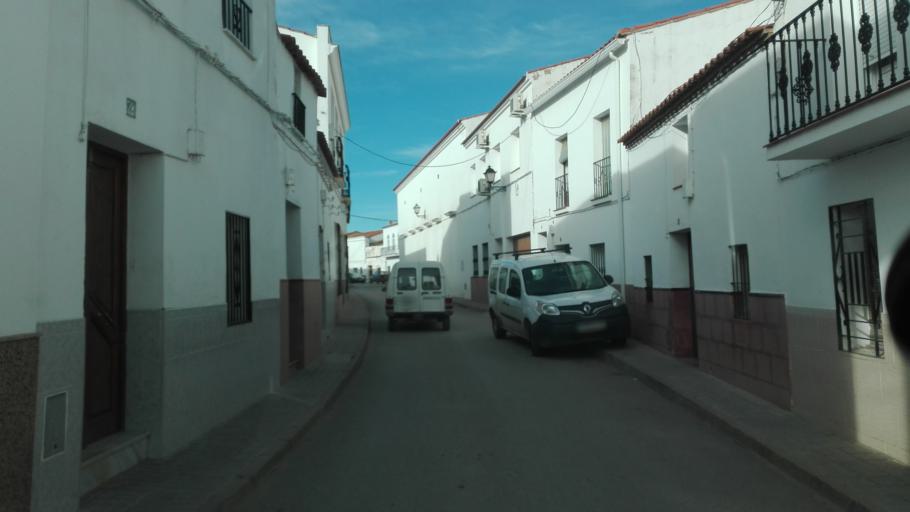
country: ES
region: Extremadura
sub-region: Provincia de Badajoz
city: Usagre
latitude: 38.3583
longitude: -6.1628
